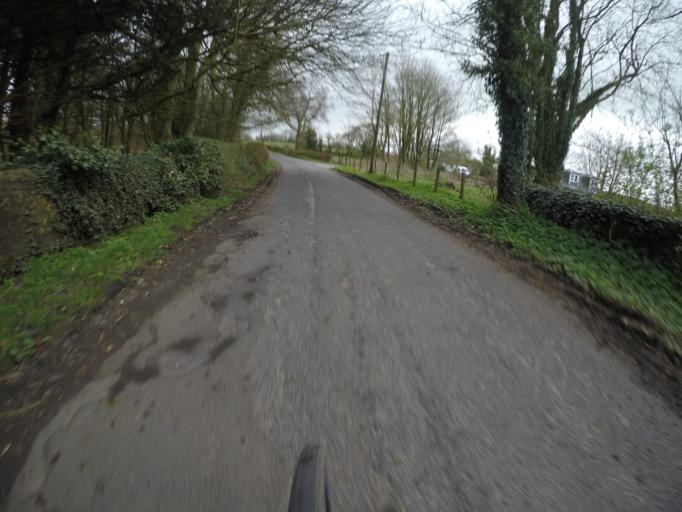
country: GB
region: Scotland
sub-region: East Ayrshire
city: Kilmaurs
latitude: 55.6702
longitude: -4.5691
